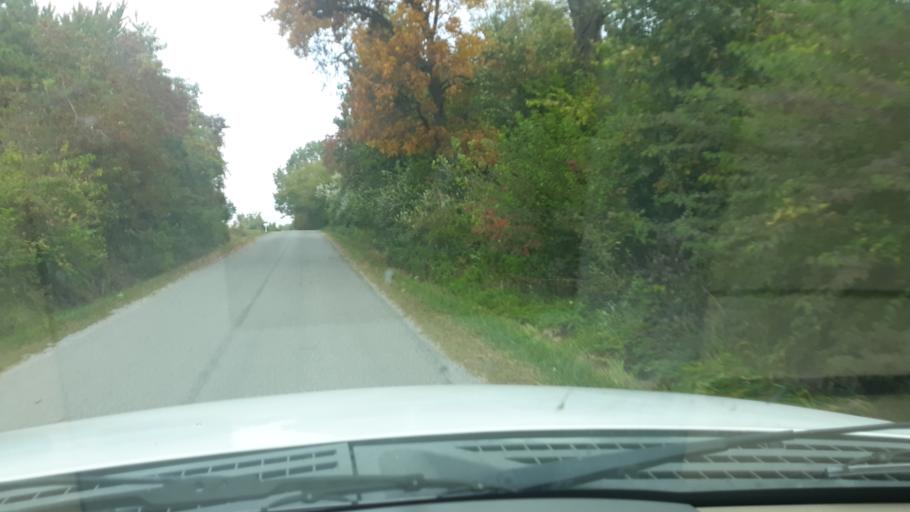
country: US
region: Illinois
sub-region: Saline County
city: Eldorado
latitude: 37.8288
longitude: -88.4848
